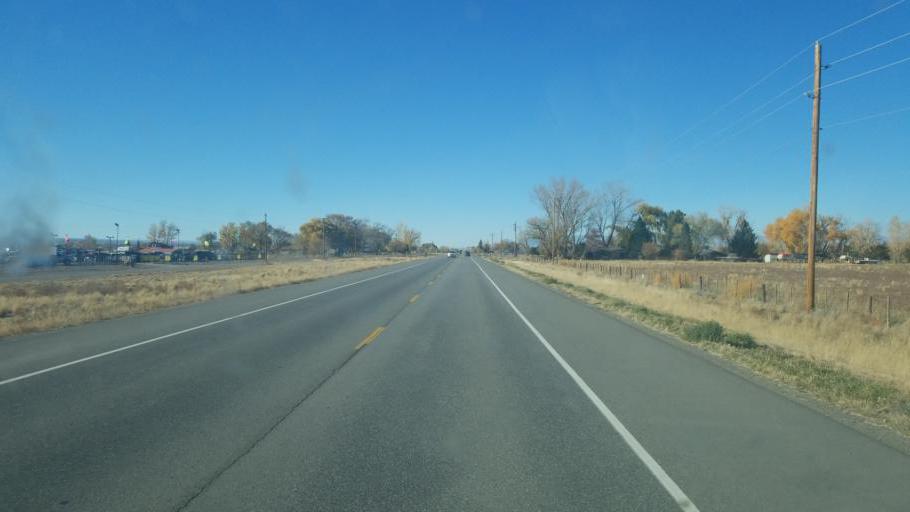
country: US
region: Colorado
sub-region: Montrose County
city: Montrose
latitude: 38.4041
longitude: -107.8413
